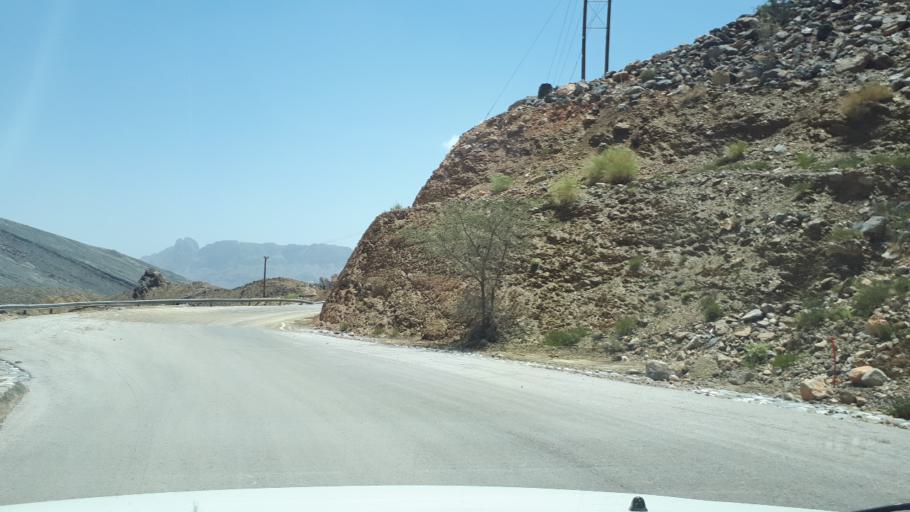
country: OM
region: Muhafazat ad Dakhiliyah
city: Bahla'
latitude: 23.2177
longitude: 57.1460
